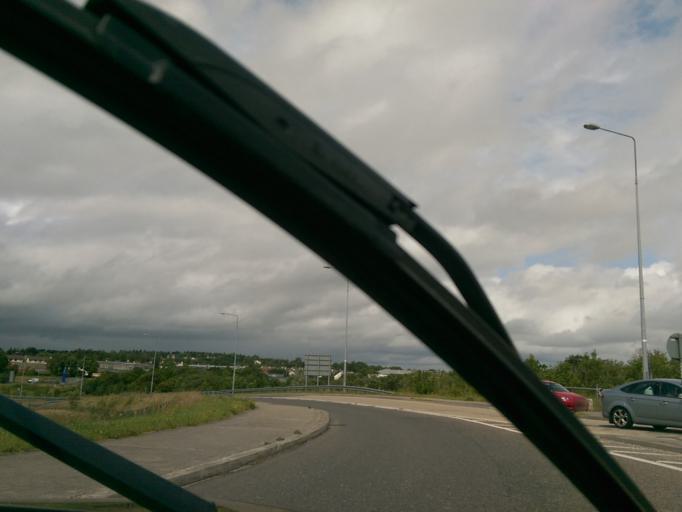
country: IE
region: Munster
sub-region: An Clar
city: Ennis
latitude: 52.8267
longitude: -8.9947
